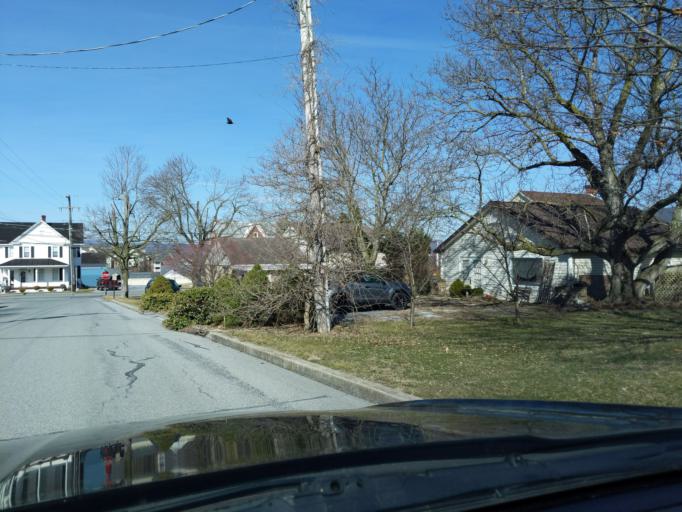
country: US
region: Pennsylvania
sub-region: Blair County
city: Martinsburg
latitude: 40.3033
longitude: -78.3284
